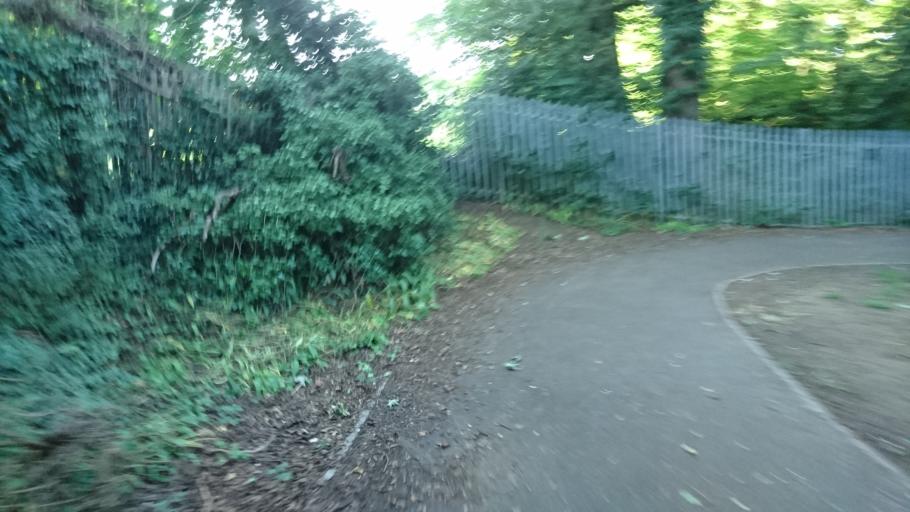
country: GB
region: England
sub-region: Greater London
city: Hendon
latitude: 51.6063
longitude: -0.2015
